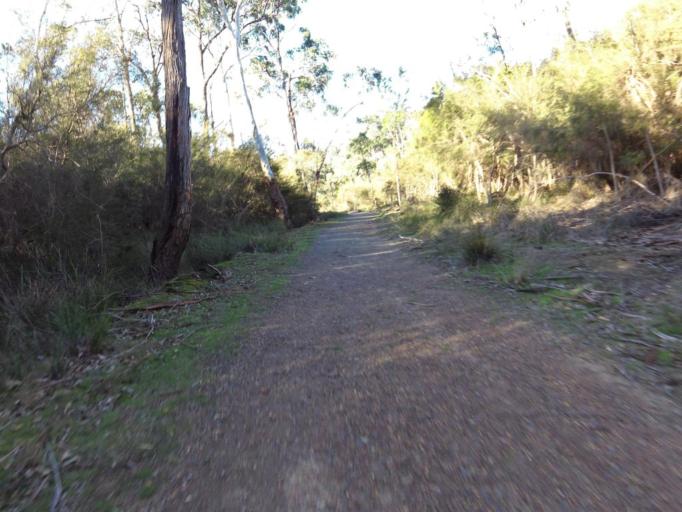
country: AU
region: Victoria
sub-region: Manningham
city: Warrandyte
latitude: -37.7329
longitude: 145.2341
